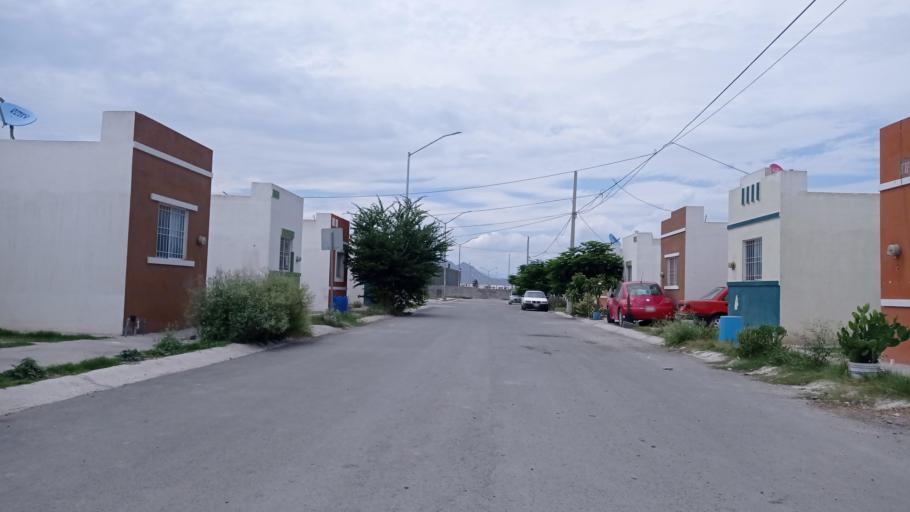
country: MX
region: Nuevo Leon
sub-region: Salinas Victoria
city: Simeprodeso (Colectivo Nuevo)
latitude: 25.8759
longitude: -100.3162
